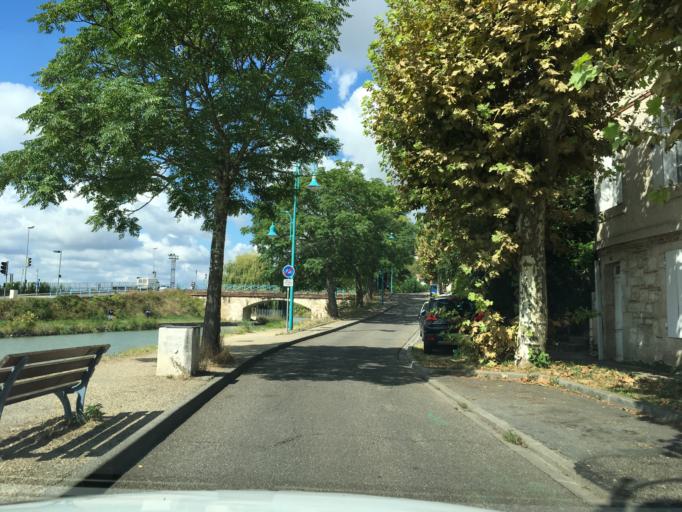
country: FR
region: Aquitaine
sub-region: Departement du Lot-et-Garonne
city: Agen
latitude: 44.2092
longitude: 0.6229
